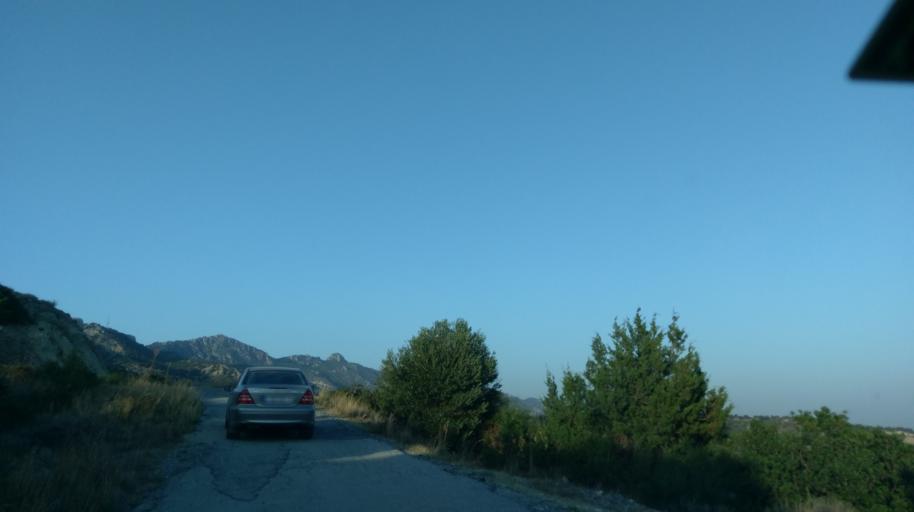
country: CY
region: Ammochostos
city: Trikomo
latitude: 35.3718
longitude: 33.9053
